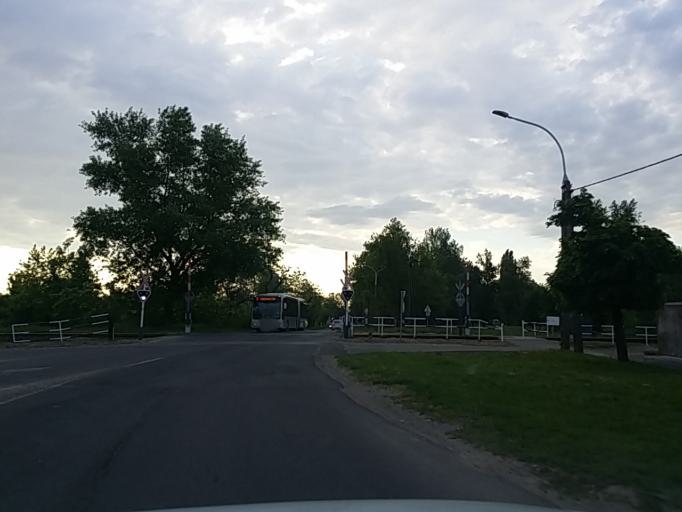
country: HU
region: Bacs-Kiskun
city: Kecskemet
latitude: 46.9002
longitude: 19.7113
